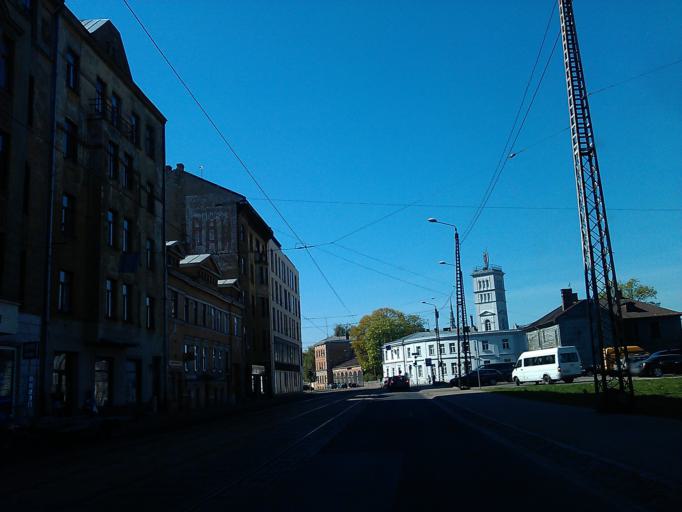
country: LV
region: Riga
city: Riga
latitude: 56.9412
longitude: 24.1204
